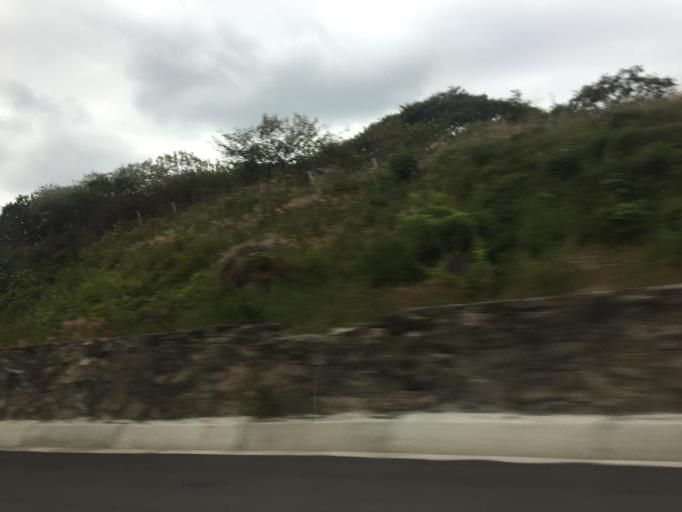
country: MX
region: Jalisco
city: Ocotlan
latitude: 20.4280
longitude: -102.7766
